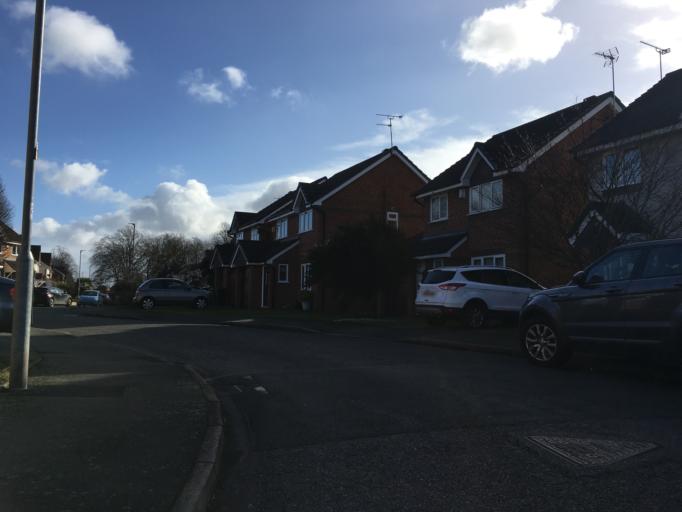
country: GB
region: England
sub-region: Cheshire West and Chester
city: Hoole
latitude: 53.1981
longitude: -2.8706
